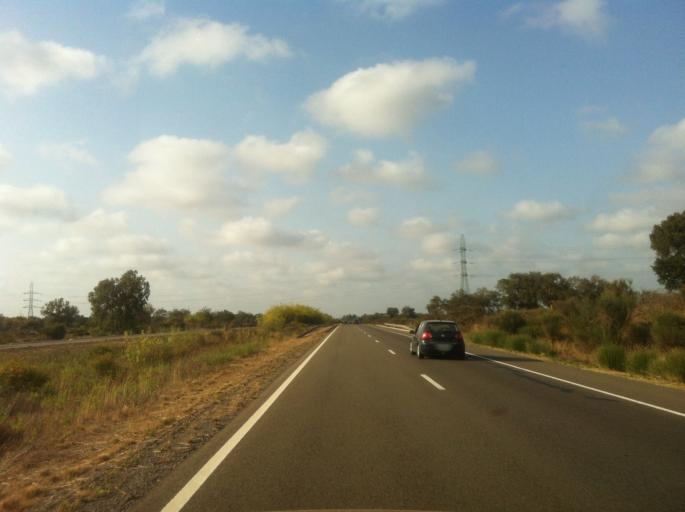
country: MA
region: Gharb-Chrarda-Beni Hssen
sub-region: Kenitra Province
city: Kenitra
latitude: 34.2267
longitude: -6.5536
